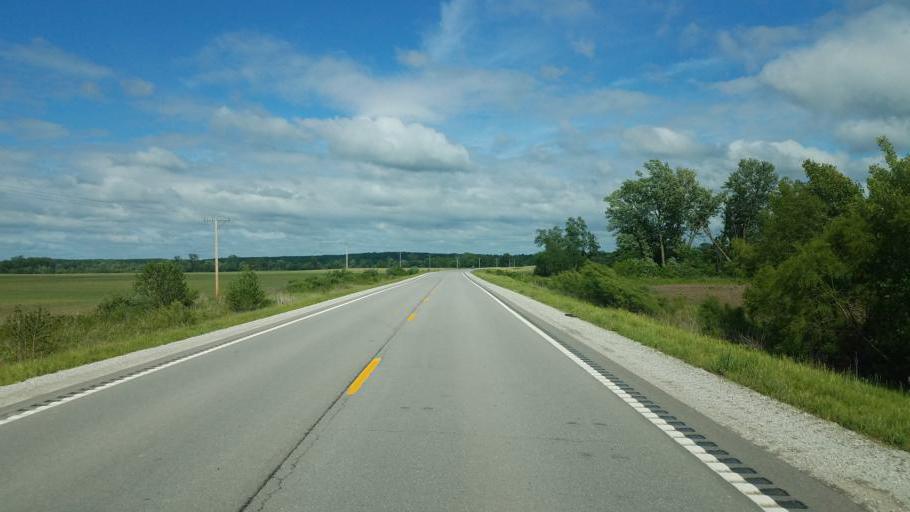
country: US
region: Missouri
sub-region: Mercer County
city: Princeton
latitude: 40.3358
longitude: -93.7797
